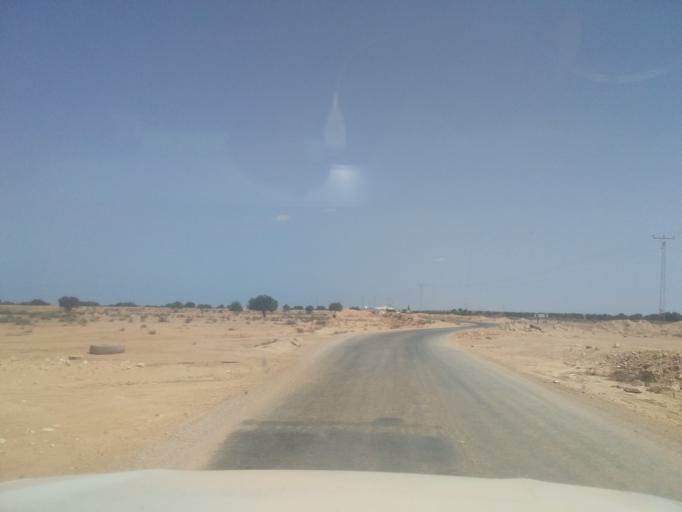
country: TN
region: Qabis
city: Matmata
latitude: 33.6065
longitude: 10.2039
